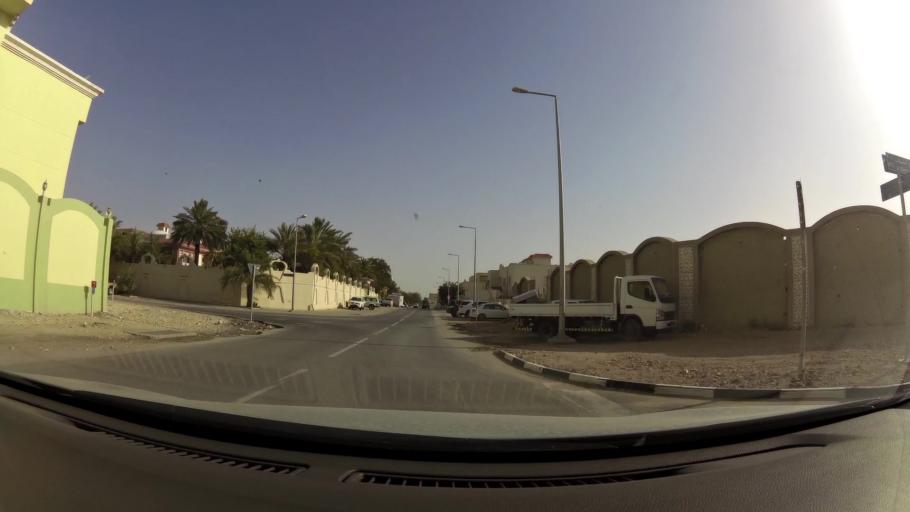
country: QA
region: Baladiyat ar Rayyan
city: Ar Rayyan
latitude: 25.3390
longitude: 51.4442
